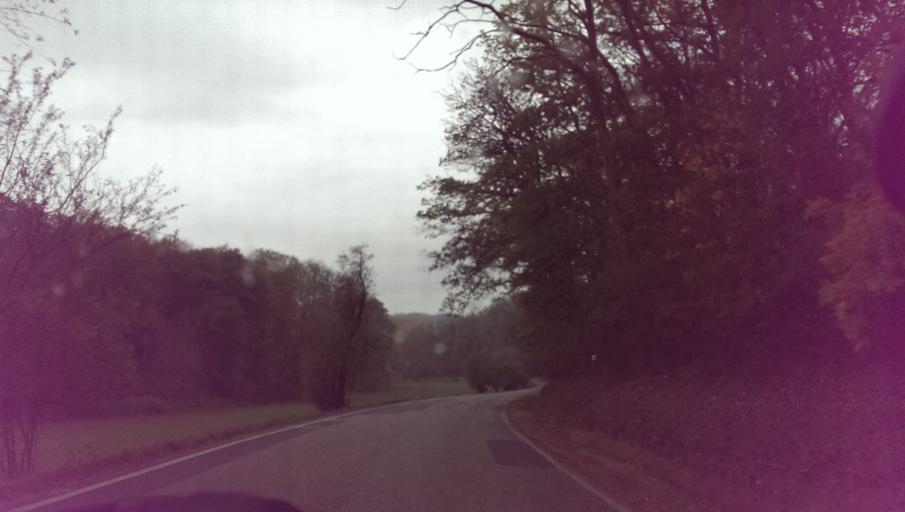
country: CZ
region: South Moravian
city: Ostopovice
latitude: 49.1461
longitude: 16.5366
